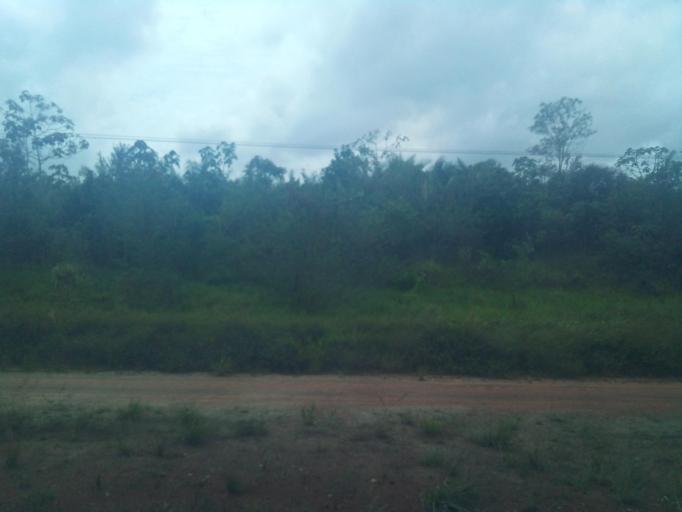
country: BR
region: Maranhao
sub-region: Itapecuru Mirim
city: Itapecuru Mirim
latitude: -3.1683
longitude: -44.3608
